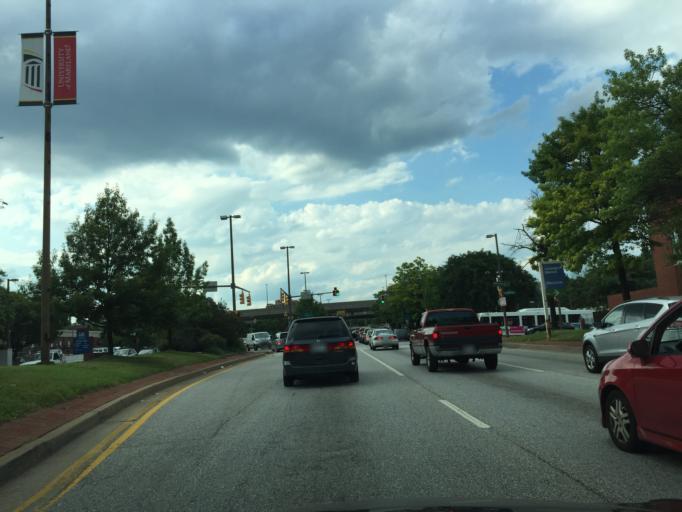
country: US
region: Maryland
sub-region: City of Baltimore
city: Baltimore
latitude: 39.2921
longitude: -76.6276
